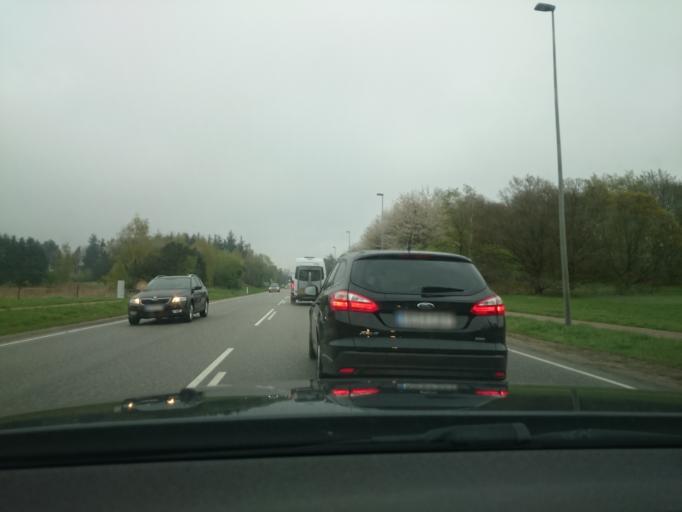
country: DK
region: Capital Region
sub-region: Ballerup Kommune
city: Ballerup
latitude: 55.7450
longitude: 12.3908
